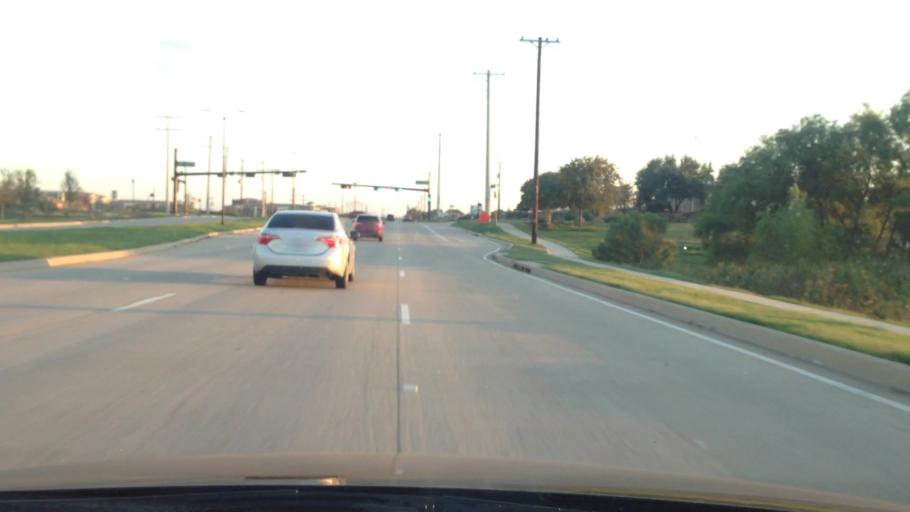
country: US
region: Texas
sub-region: Denton County
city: The Colony
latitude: 33.1377
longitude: -96.8907
